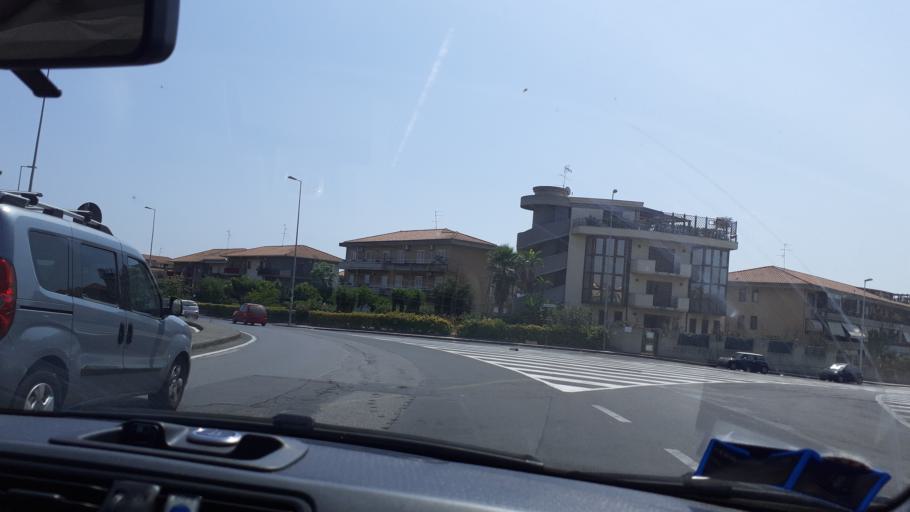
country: IT
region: Sicily
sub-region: Catania
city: Misterbianco
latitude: 37.5135
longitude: 15.0543
